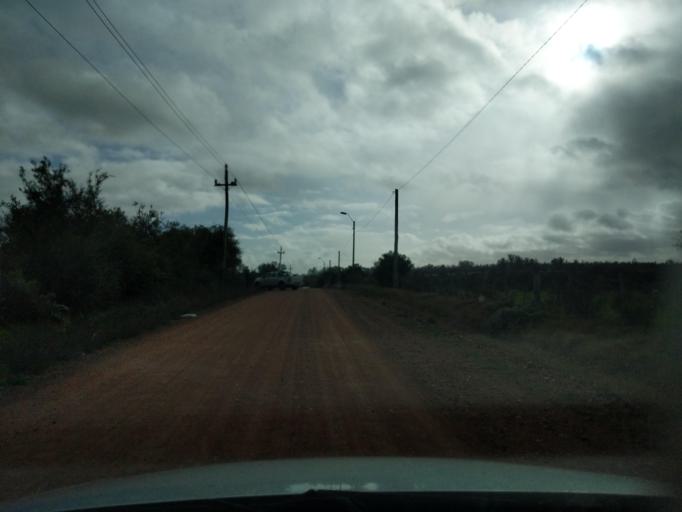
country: UY
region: Florida
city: Florida
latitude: -34.0634
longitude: -56.2176
